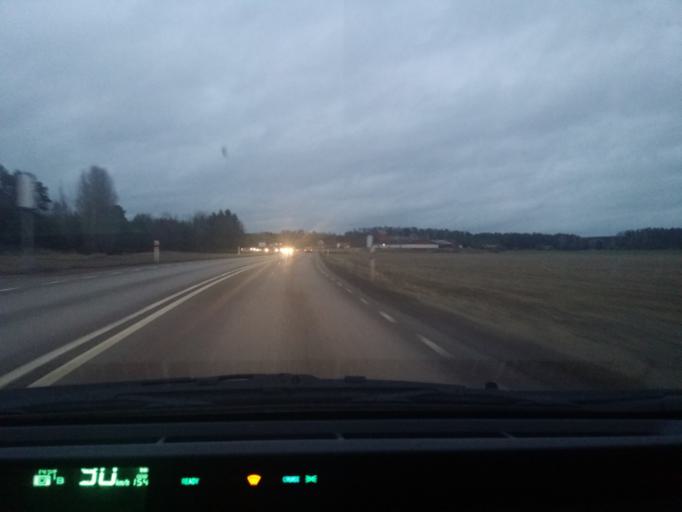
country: SE
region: Vaestmanland
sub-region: Hallstahammars Kommun
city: Kolback
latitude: 59.5588
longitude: 16.3418
